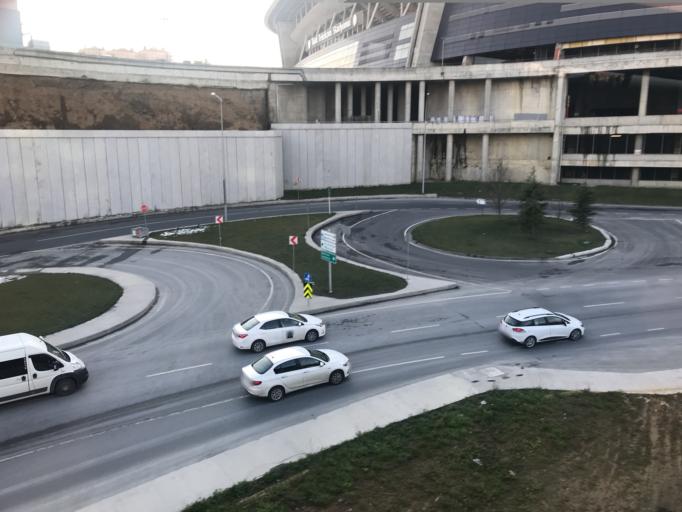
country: TR
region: Istanbul
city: Sisli
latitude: 41.1035
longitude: 28.9937
